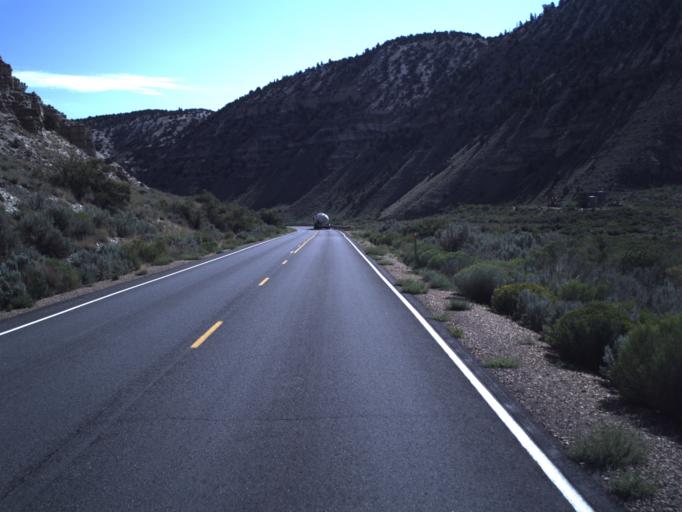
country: US
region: Utah
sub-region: Duchesne County
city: Duchesne
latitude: 40.0474
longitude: -110.5313
